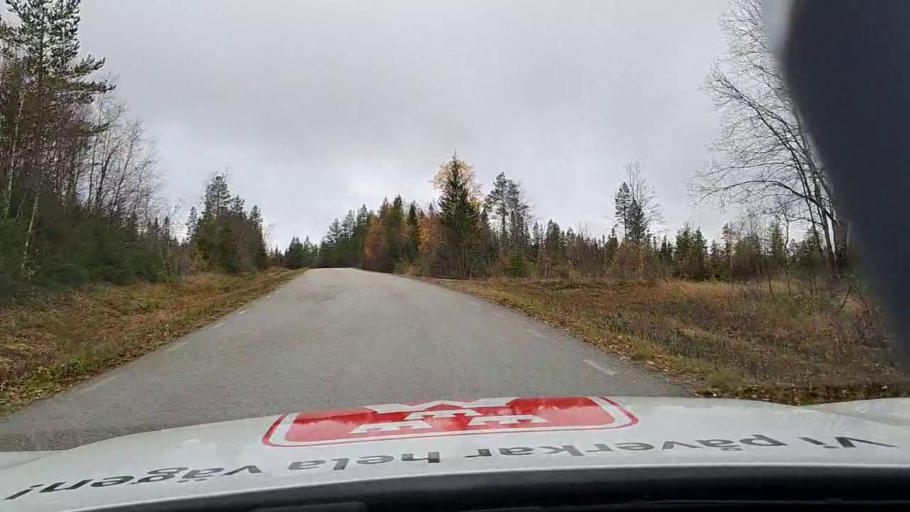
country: SE
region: Jaemtland
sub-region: Bergs Kommun
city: Hoverberg
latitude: 63.0434
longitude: 13.9954
